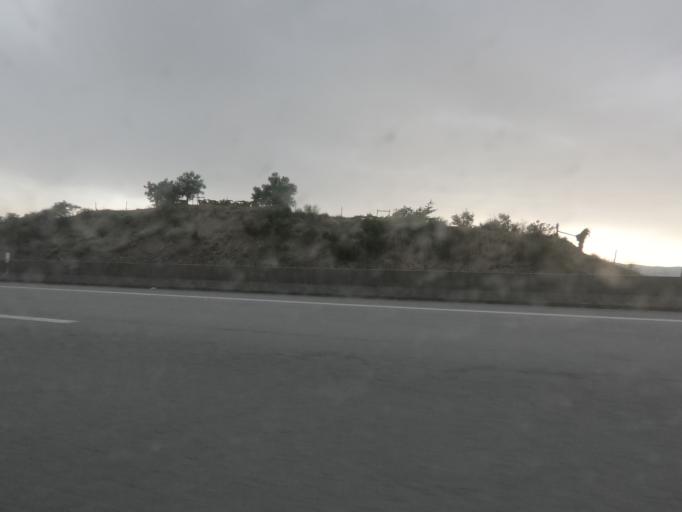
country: PT
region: Vila Real
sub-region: Peso da Regua
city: Peso da Regua
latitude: 41.2010
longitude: -7.7473
